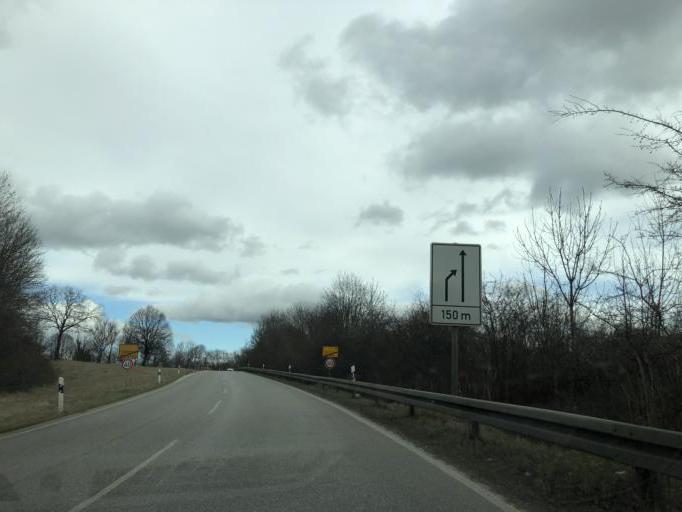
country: DE
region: Bavaria
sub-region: Upper Bavaria
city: Unterfoehring
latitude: 48.1857
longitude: 11.6147
